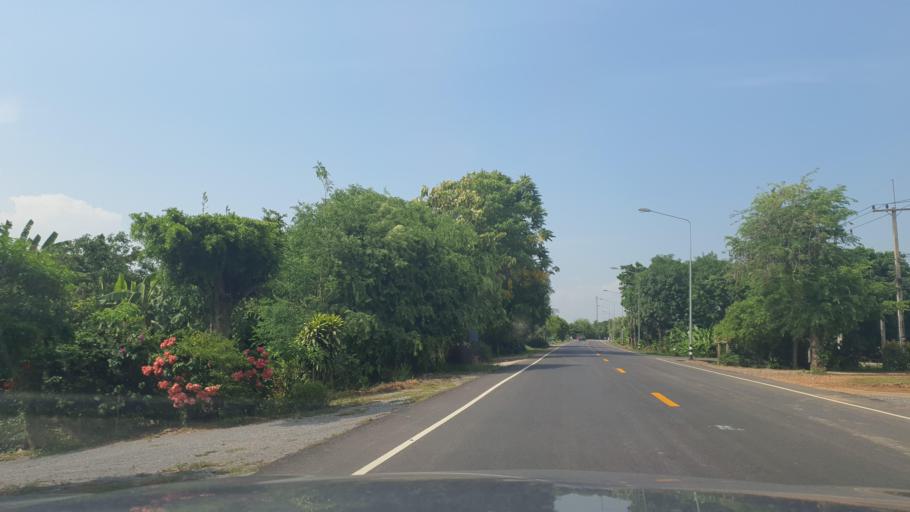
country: TH
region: Sukhothai
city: Si Samrong
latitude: 17.1593
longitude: 99.8280
